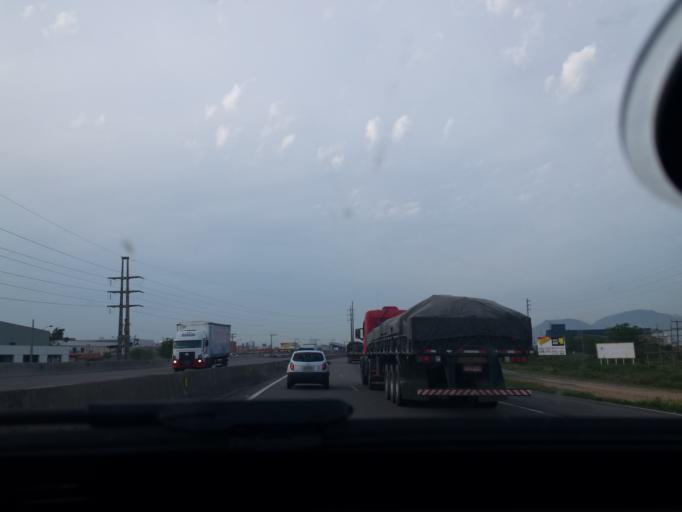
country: BR
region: Santa Catarina
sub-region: Tubarao
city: Tubarao
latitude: -28.4631
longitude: -48.9922
